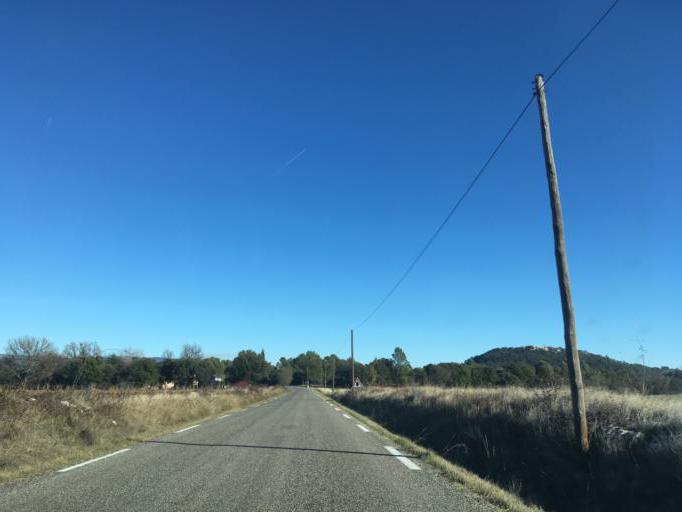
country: FR
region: Provence-Alpes-Cote d'Azur
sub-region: Departement du Var
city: Barjols
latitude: 43.5920
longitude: 6.0790
